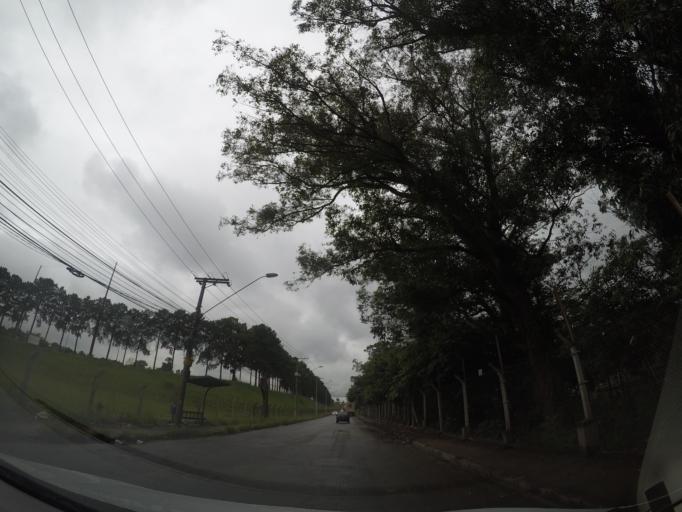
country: BR
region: Sao Paulo
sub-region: Guarulhos
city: Guarulhos
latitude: -23.4693
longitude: -46.4528
